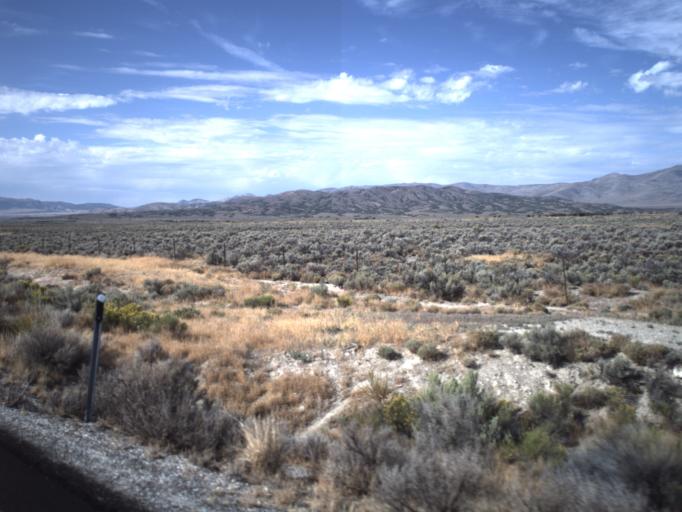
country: US
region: Idaho
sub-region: Cassia County
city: Burley
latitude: 41.6984
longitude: -113.5345
